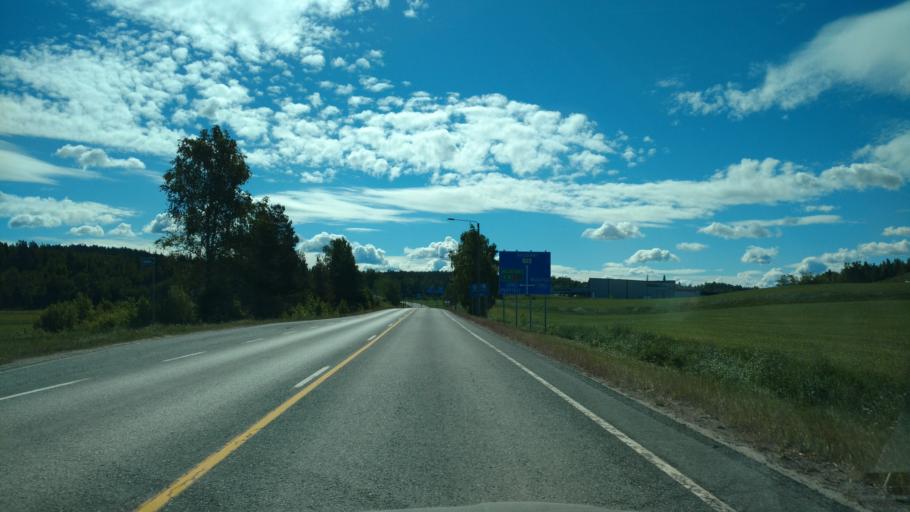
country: FI
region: Varsinais-Suomi
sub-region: Salo
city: Muurla
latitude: 60.3759
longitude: 23.3087
